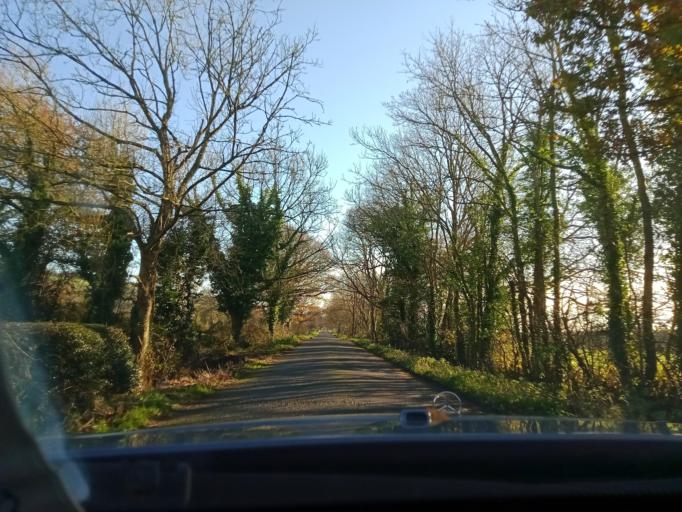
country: IE
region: Leinster
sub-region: Kilkenny
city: Piltown
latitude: 52.3531
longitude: -7.2918
